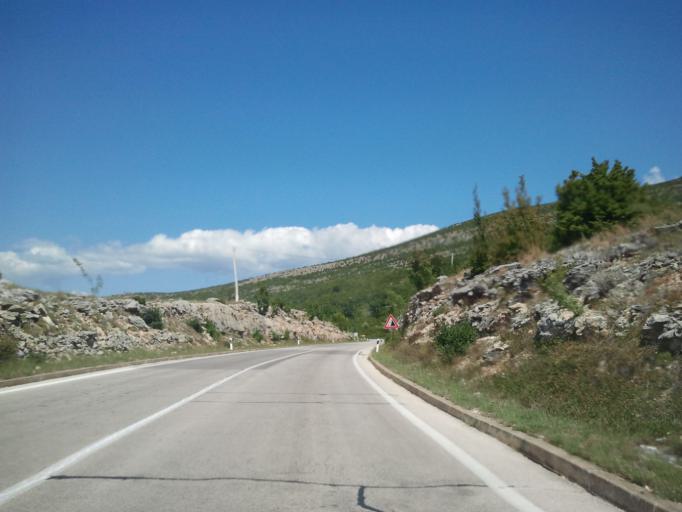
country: HR
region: Zadarska
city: Krusevo
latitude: 44.1594
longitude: 15.6252
